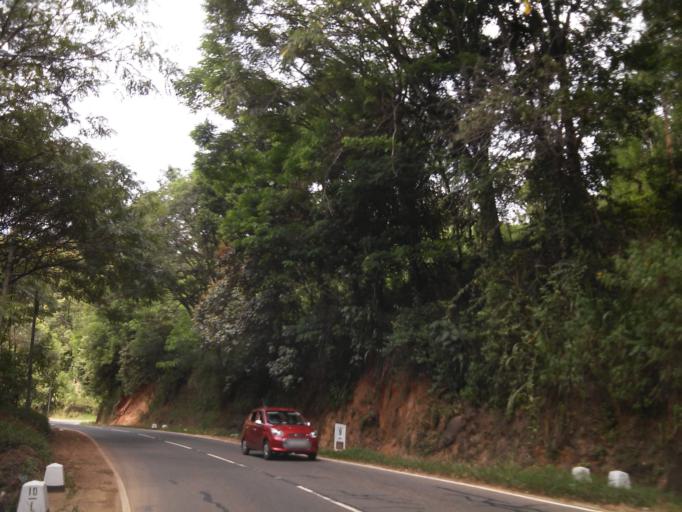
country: LK
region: Uva
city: Haputale
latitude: 6.8699
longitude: 80.9515
